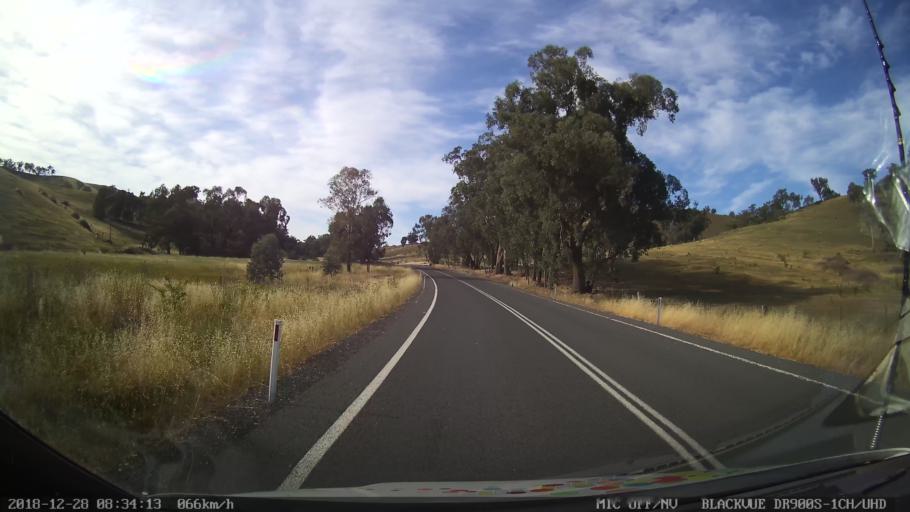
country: AU
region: New South Wales
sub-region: Blayney
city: Blayney
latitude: -33.9726
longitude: 149.3085
